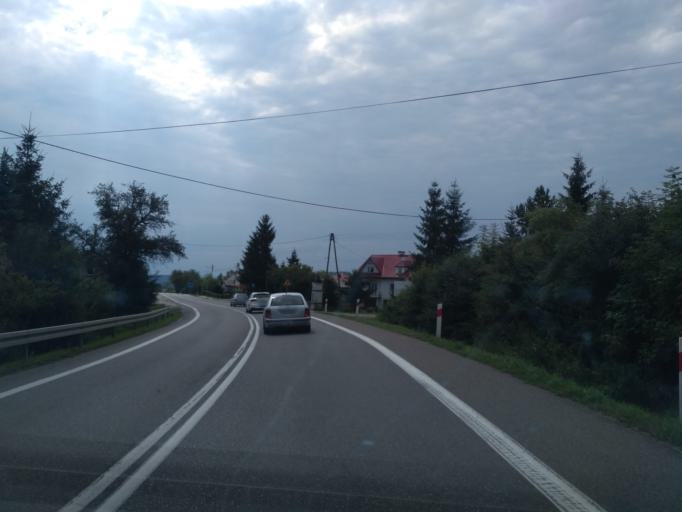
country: PL
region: Subcarpathian Voivodeship
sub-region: Powiat sanocki
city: Strachocina
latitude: 49.6278
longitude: 22.0969
